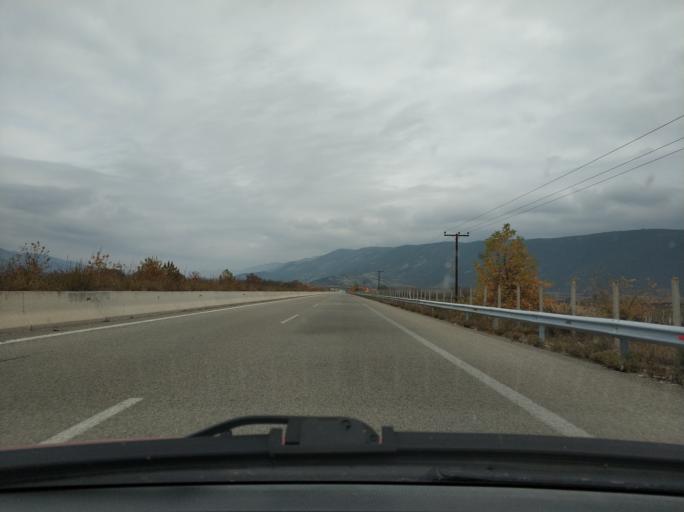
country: GR
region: Central Macedonia
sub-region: Nomos Serron
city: Rodolivos
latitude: 40.8226
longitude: 24.0699
